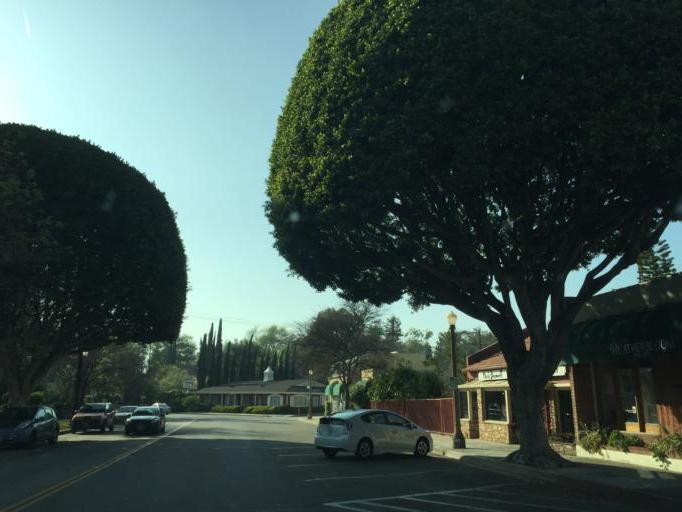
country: US
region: California
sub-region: Los Angeles County
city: South Pasadena
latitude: 34.1163
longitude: -118.1394
